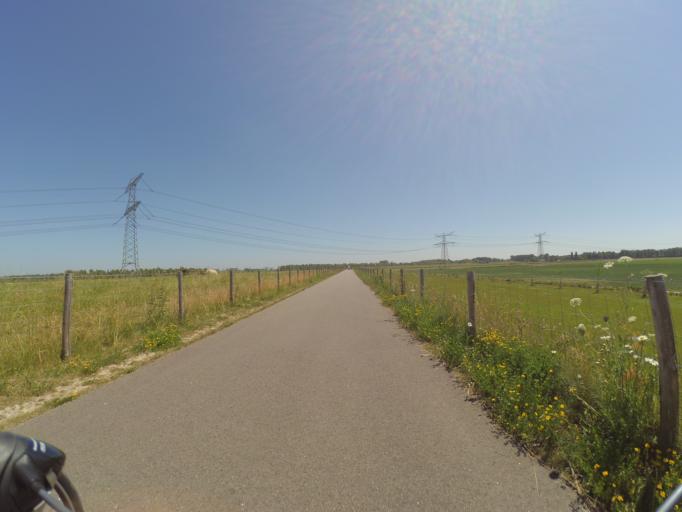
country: NL
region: South Holland
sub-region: Gemeente Sliedrecht
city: Sliedrecht
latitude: 51.7967
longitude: 4.7429
